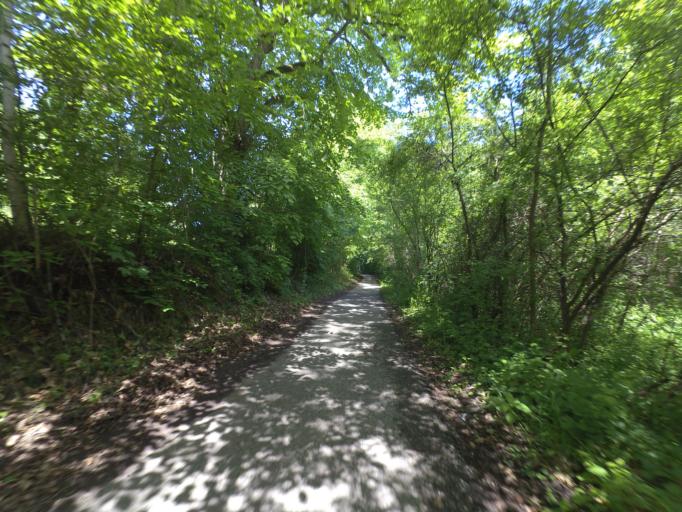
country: DE
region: Bavaria
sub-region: Upper Bavaria
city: Petting
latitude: 47.9321
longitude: 12.7770
